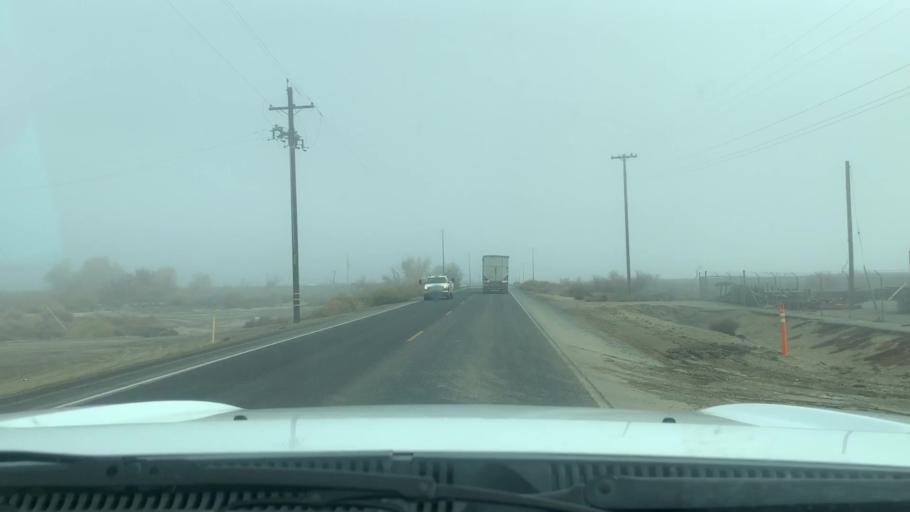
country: US
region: California
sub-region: Kern County
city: Lost Hills
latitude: 35.4994
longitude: -119.6202
